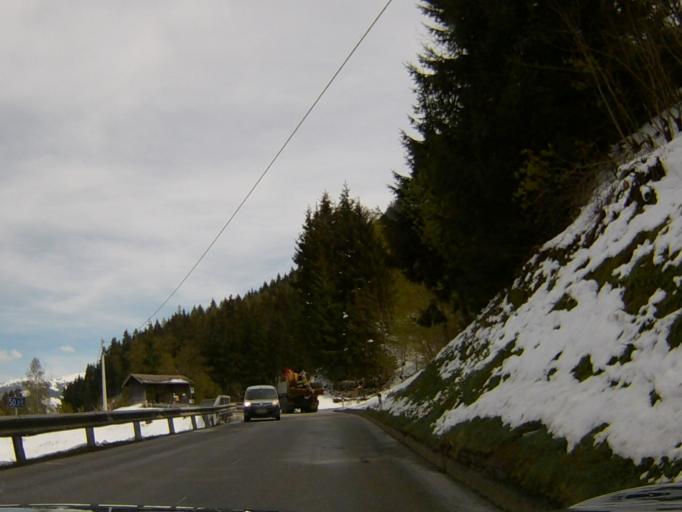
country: AT
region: Tyrol
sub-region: Politischer Bezirk Schwaz
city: Gerlosberg
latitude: 47.2123
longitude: 11.9365
